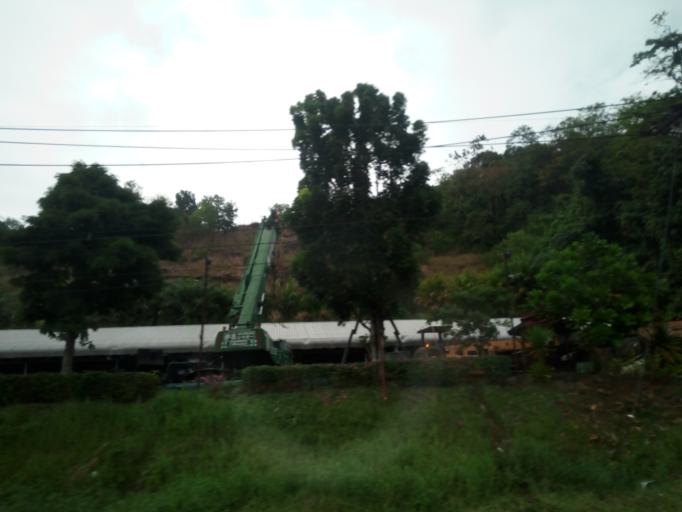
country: TH
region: Phuket
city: Ban Ko Kaeo
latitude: 7.9414
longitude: 98.3807
